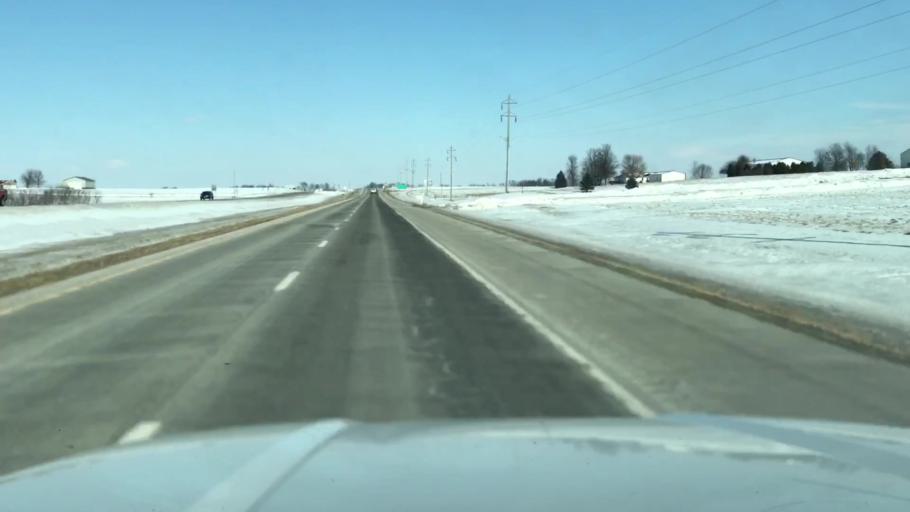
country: US
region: Missouri
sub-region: Nodaway County
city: Maryville
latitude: 40.2550
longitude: -94.8669
